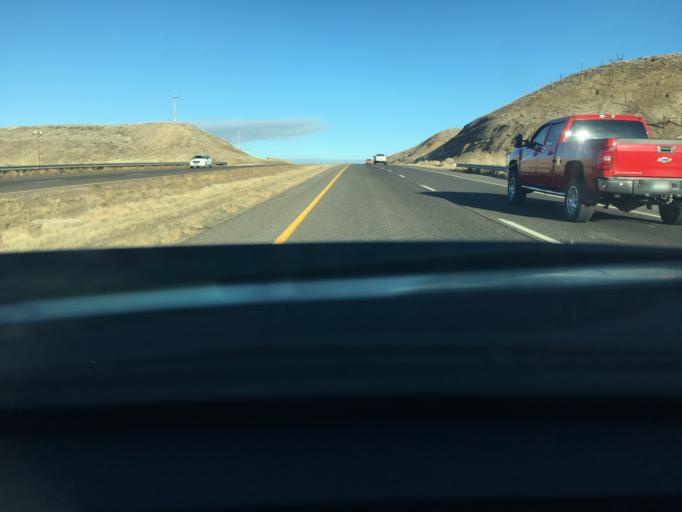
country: US
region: Colorado
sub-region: Mesa County
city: Clifton
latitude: 38.9213
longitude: -108.3807
